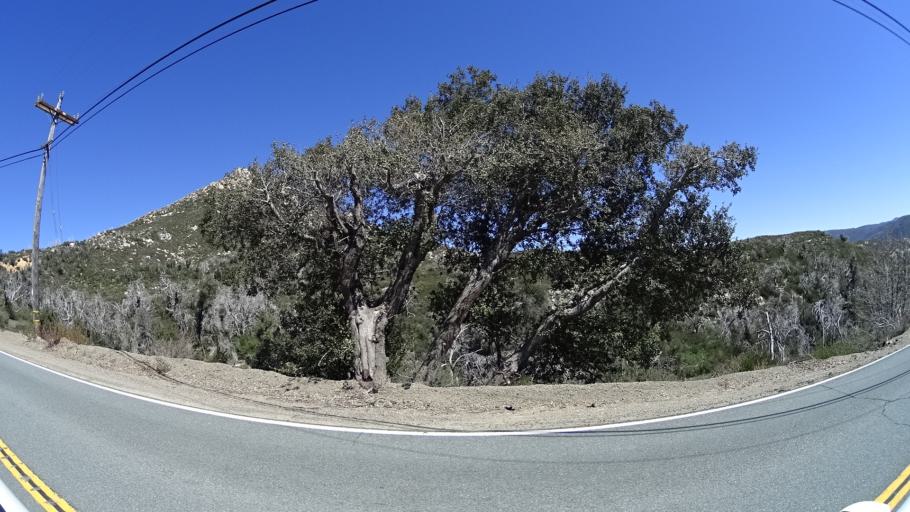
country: US
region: California
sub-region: San Diego County
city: Descanso
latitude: 32.9548
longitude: -116.5772
